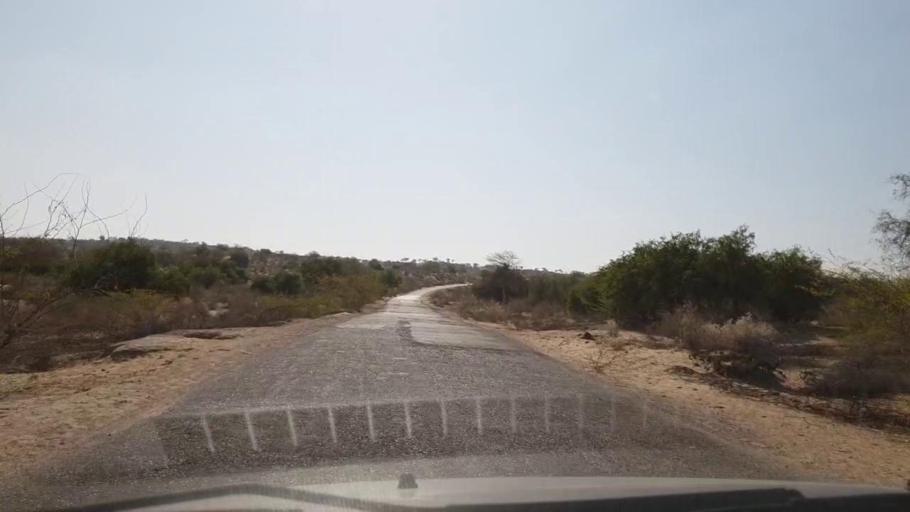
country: PK
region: Sindh
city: Mithi
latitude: 24.6367
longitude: 69.7428
